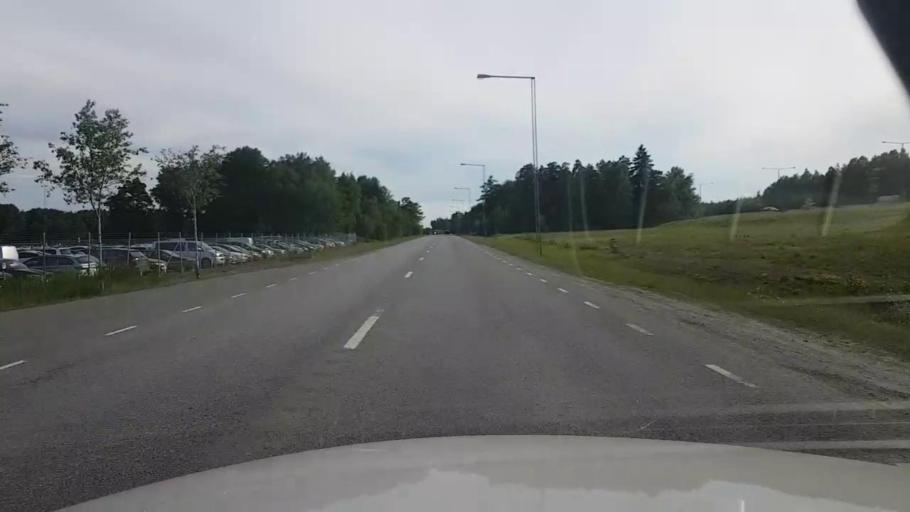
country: SE
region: Stockholm
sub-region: Sigtuna Kommun
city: Rosersberg
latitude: 59.6370
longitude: 17.9367
